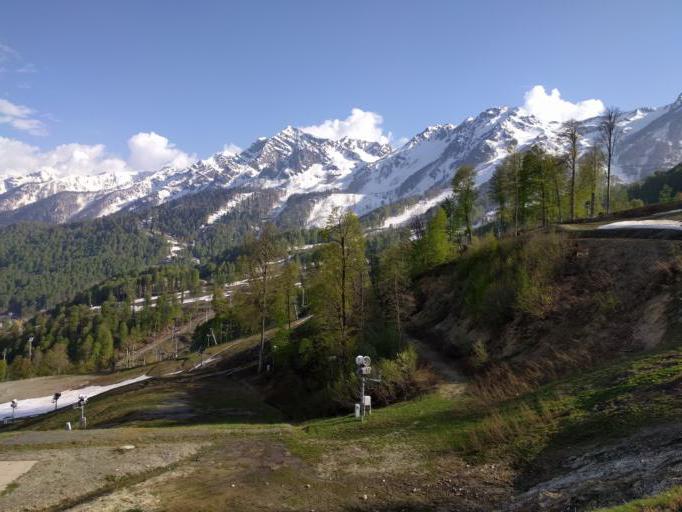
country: RU
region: Krasnodarskiy
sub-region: Sochi City
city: Krasnaya Polyana
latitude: 43.6574
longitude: 40.3211
